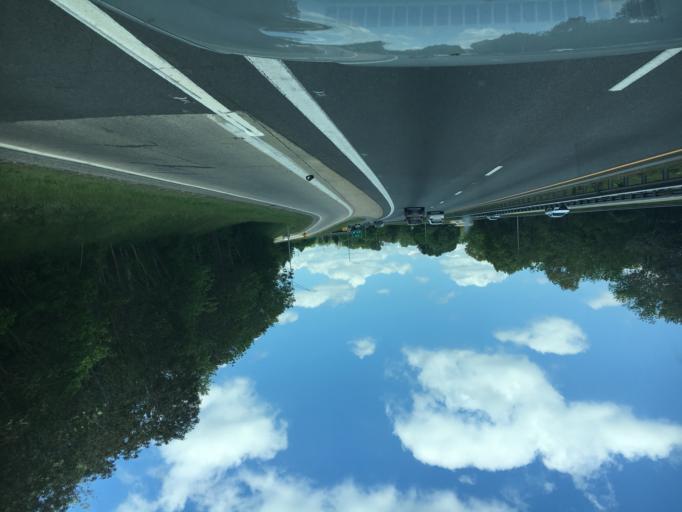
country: US
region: North Carolina
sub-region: Buncombe County
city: Woodfin
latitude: 35.6275
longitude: -82.5793
